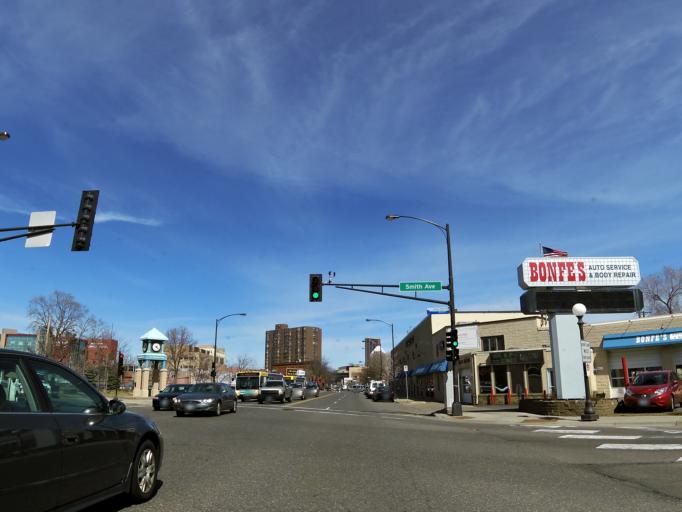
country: US
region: Minnesota
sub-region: Ramsey County
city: Saint Paul
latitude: 44.9366
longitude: -93.1115
